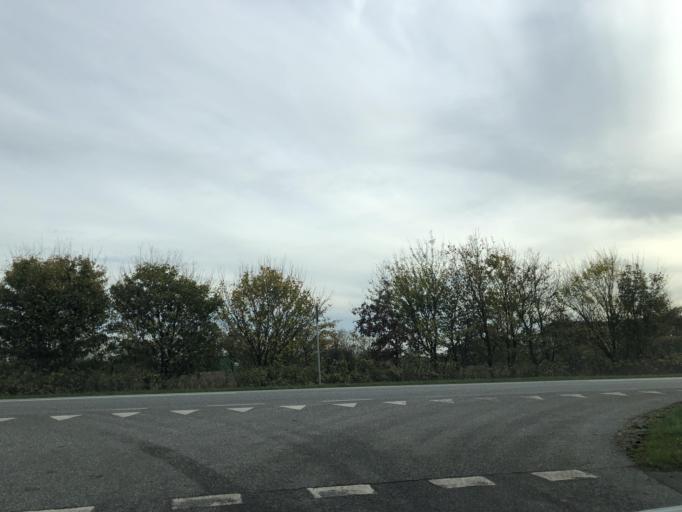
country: DK
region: South Denmark
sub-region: Esbjerg Kommune
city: Ribe
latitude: 55.3014
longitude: 8.7434
